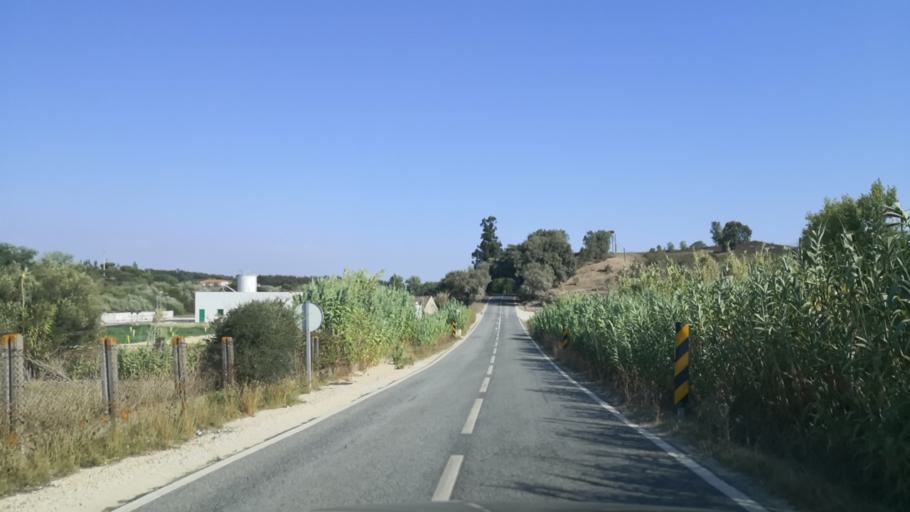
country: PT
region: Santarem
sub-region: Benavente
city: Poceirao
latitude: 38.7680
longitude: -8.6227
